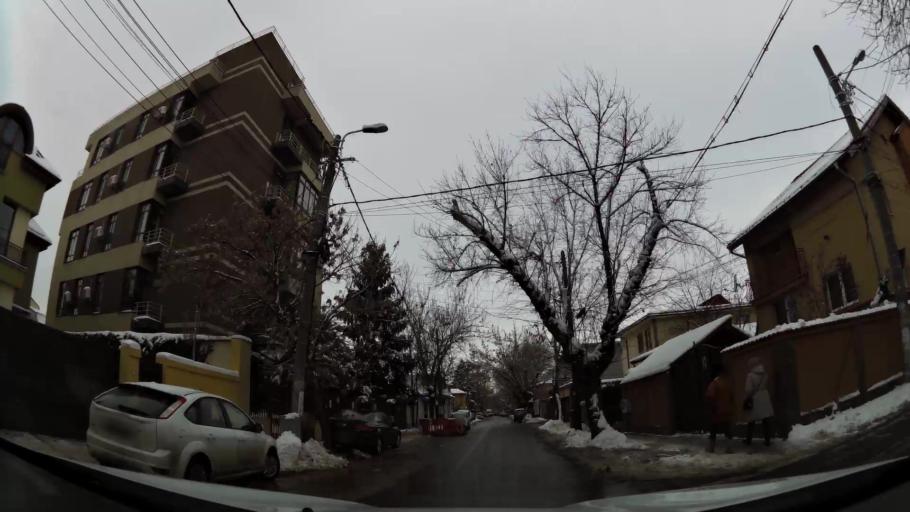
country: RO
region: Bucuresti
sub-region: Municipiul Bucuresti
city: Bucuresti
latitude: 44.3967
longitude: 26.1016
